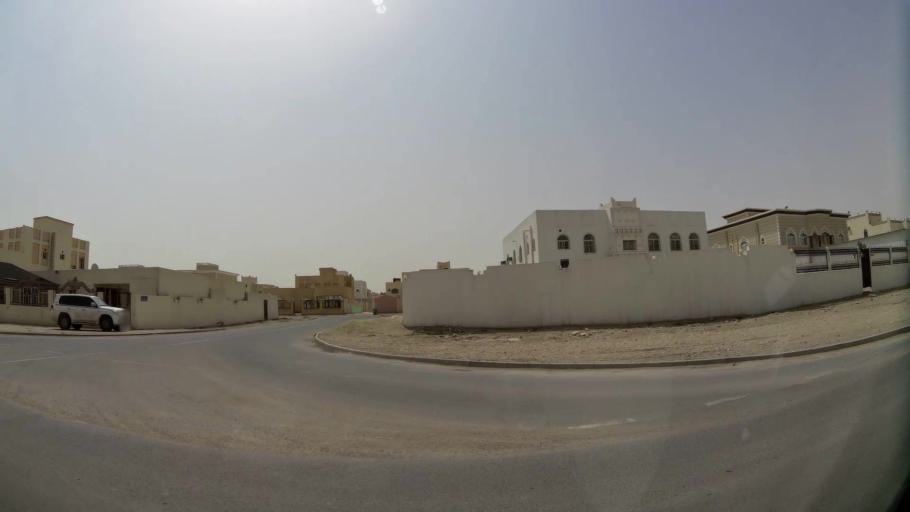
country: QA
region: Baladiyat ar Rayyan
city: Ar Rayyan
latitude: 25.2506
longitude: 51.3722
